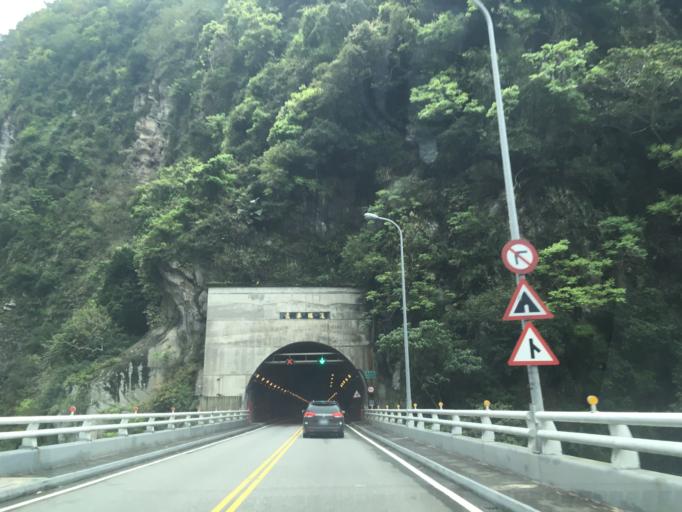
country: TW
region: Taiwan
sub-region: Hualien
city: Hualian
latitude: 24.1601
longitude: 121.6101
